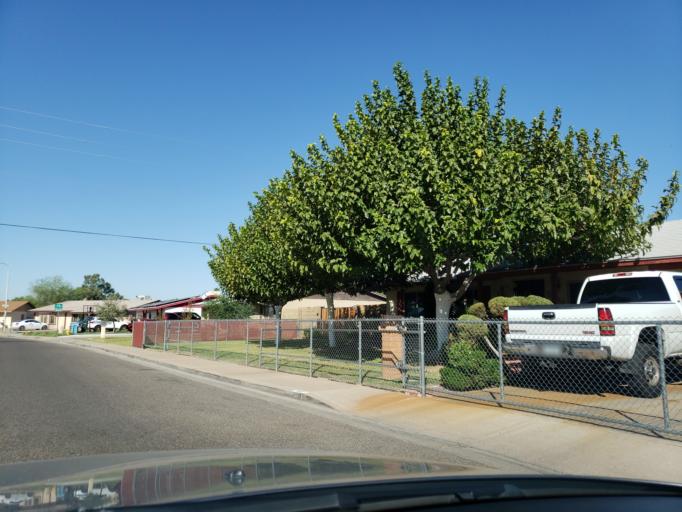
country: US
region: Arizona
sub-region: Maricopa County
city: Glendale
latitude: 33.5007
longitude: -112.2288
